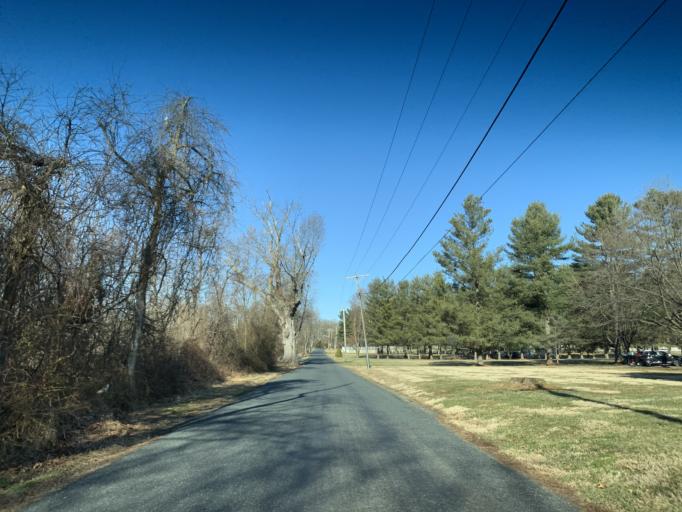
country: US
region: Maryland
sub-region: Harford County
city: South Bel Air
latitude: 39.6246
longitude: -76.2726
